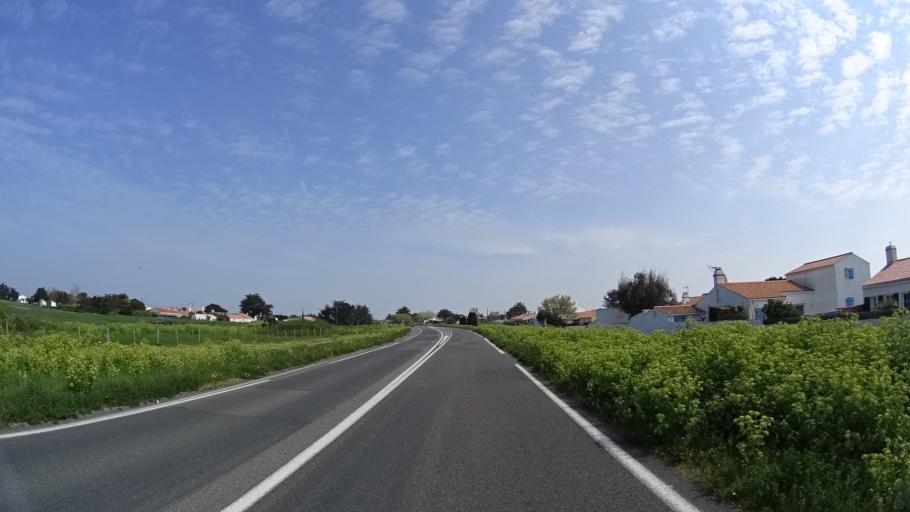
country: FR
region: Pays de la Loire
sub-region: Departement de la Vendee
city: La Gueriniere
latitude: 46.9668
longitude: -2.2511
